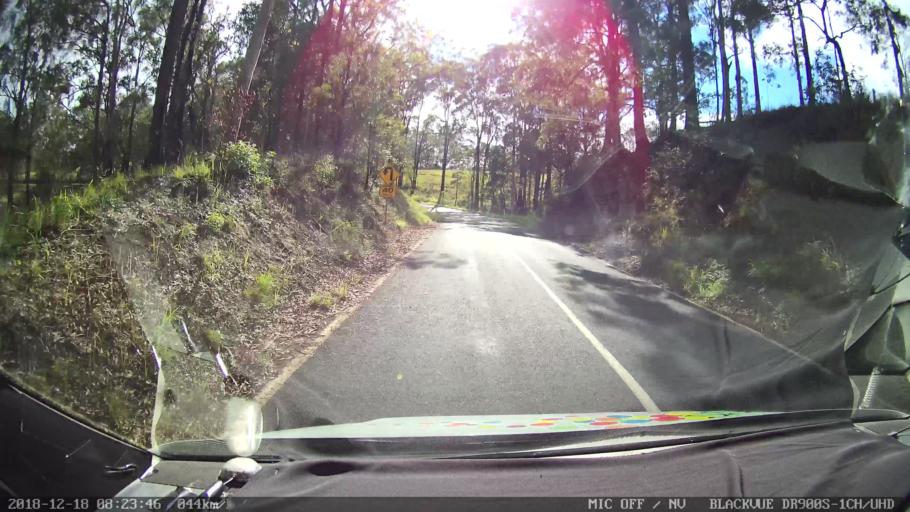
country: AU
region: New South Wales
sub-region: Kyogle
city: Kyogle
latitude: -28.3257
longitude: 152.7313
